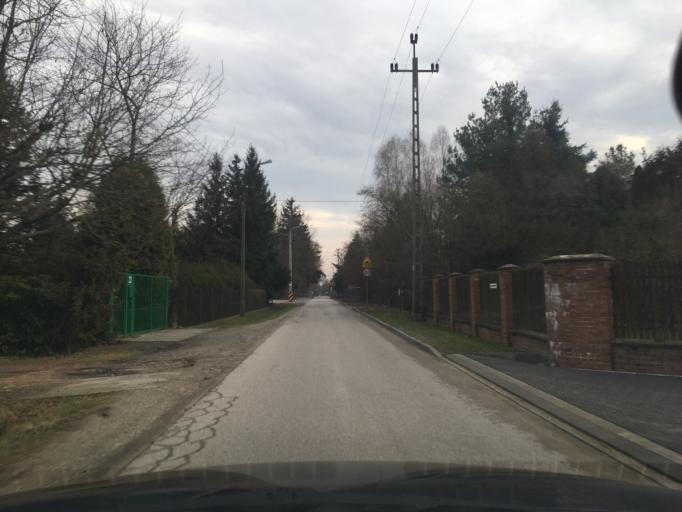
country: PL
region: Masovian Voivodeship
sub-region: Powiat piaseczynski
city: Lesznowola
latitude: 52.0387
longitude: 20.9544
